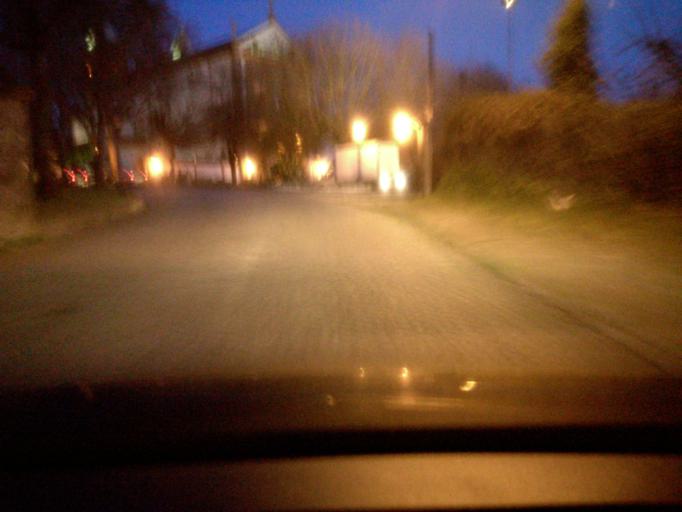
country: PT
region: Porto
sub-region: Maia
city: Gemunde
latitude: 41.2456
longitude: -8.6516
